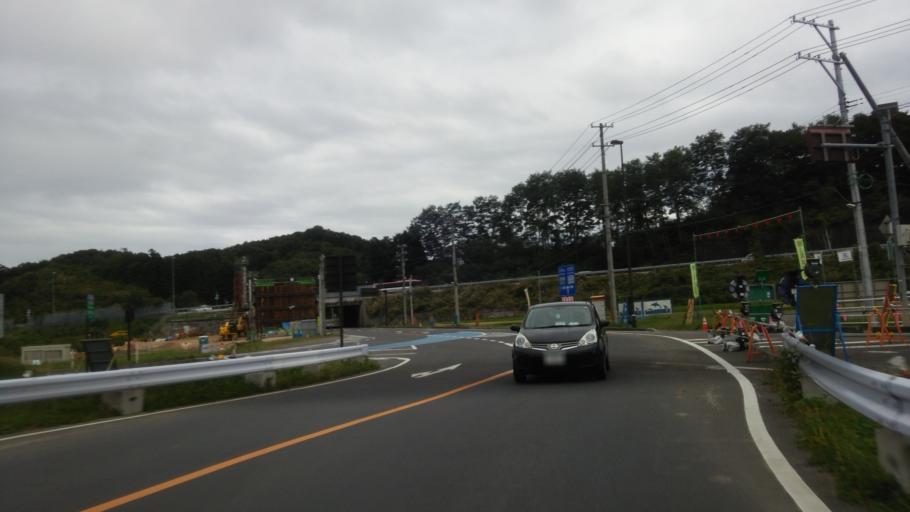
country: JP
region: Fukushima
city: Sukagawa
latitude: 37.1491
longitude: 140.2180
